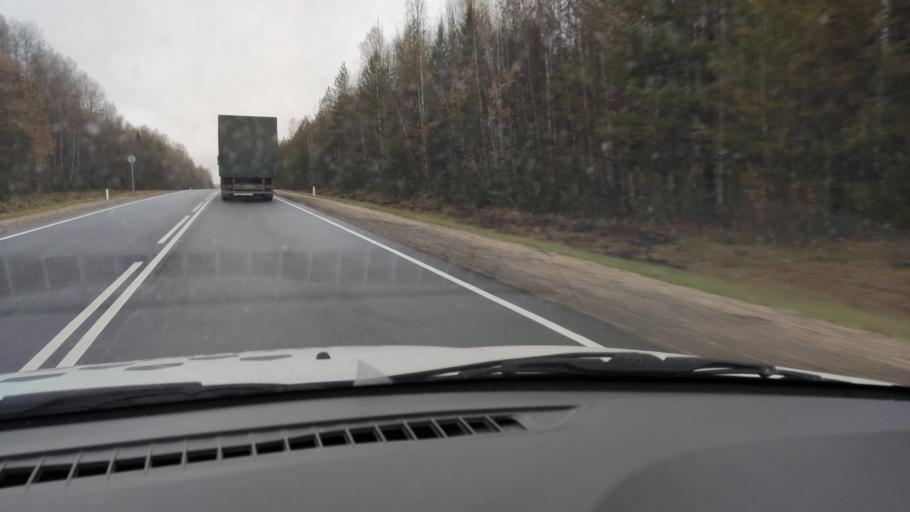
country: RU
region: Kirov
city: Chernaya Kholunitsa
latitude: 58.7967
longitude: 51.8725
